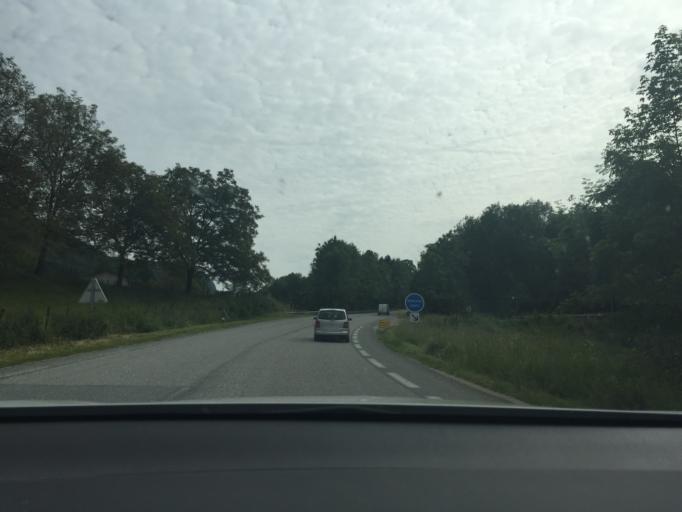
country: FR
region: Rhone-Alpes
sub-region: Departement de la Savoie
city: Vimines
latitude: 45.4766
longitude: 5.8270
